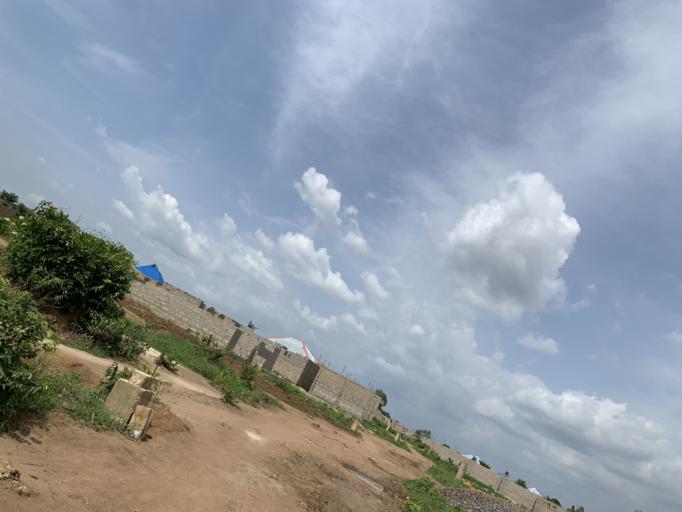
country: SL
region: Western Area
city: Waterloo
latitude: 8.3533
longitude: -13.0461
